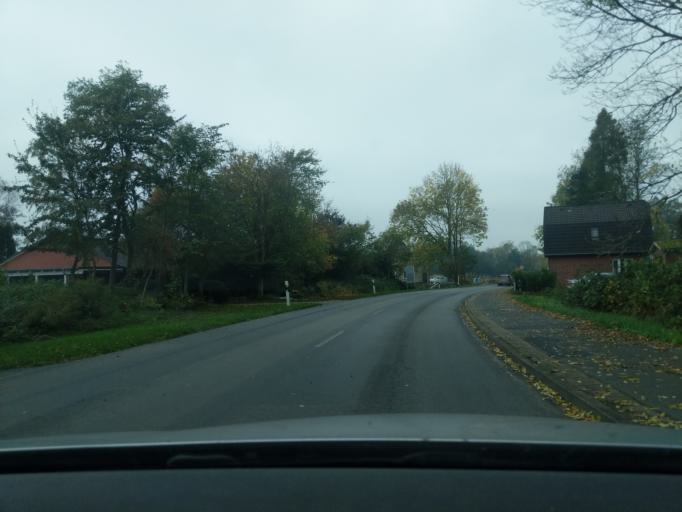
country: DE
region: Lower Saxony
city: Otterndorf
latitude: 53.8131
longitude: 8.8829
